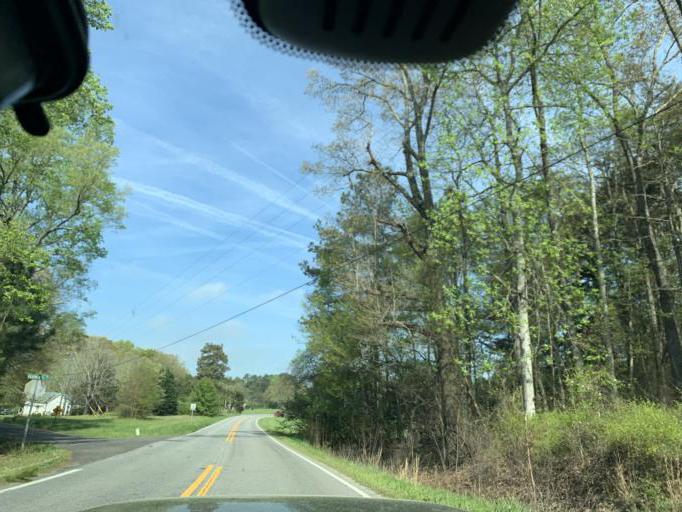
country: US
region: Georgia
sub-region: Forsyth County
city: Cumming
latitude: 34.2173
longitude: -84.0816
